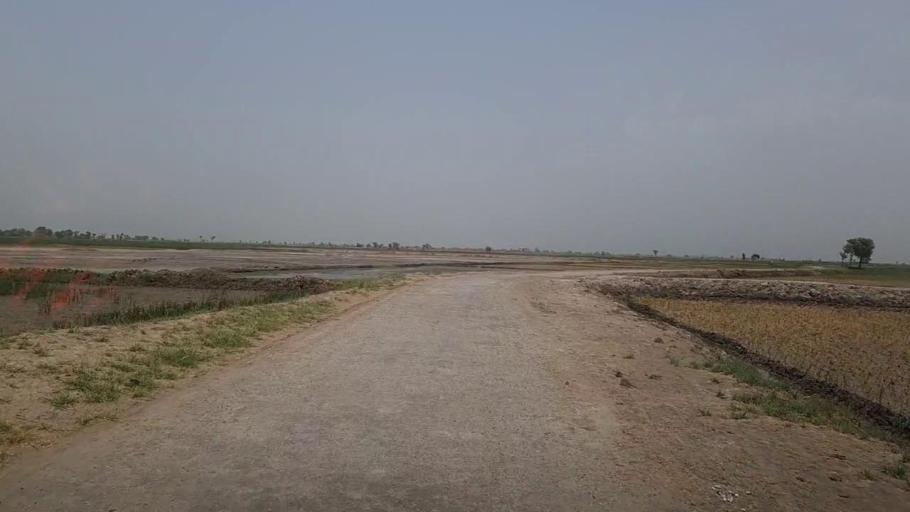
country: PK
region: Sindh
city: Sita Road
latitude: 27.0690
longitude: 67.8542
